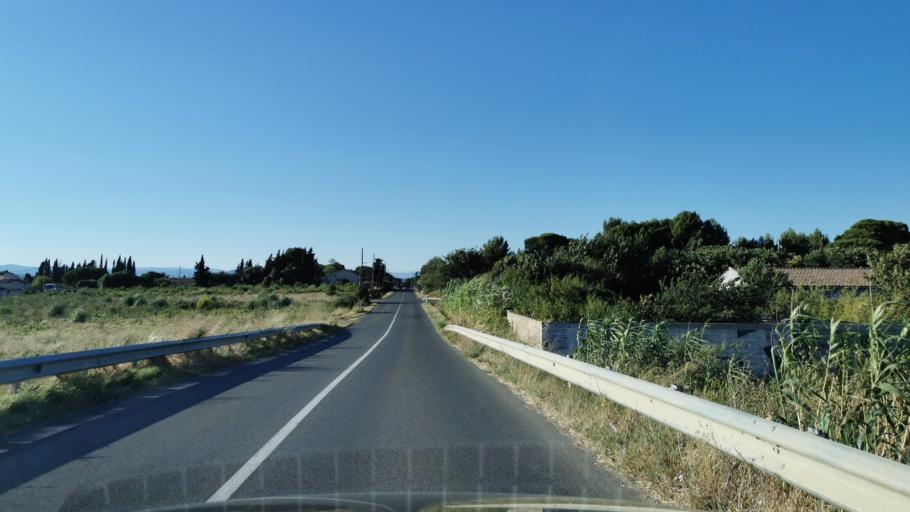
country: FR
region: Languedoc-Roussillon
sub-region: Departement de l'Aude
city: Ouveillan
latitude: 43.2636
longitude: 2.9955
